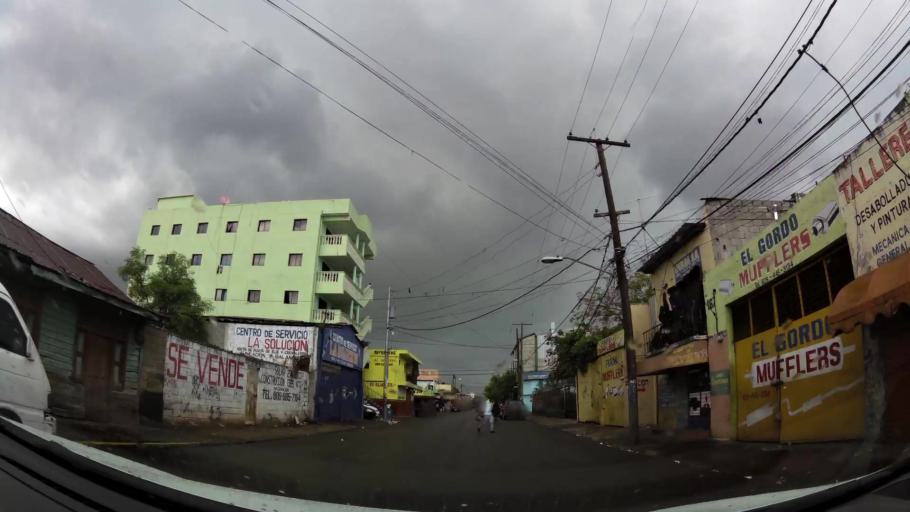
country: DO
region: Nacional
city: Ensanche Luperon
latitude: 18.4931
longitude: -69.9079
